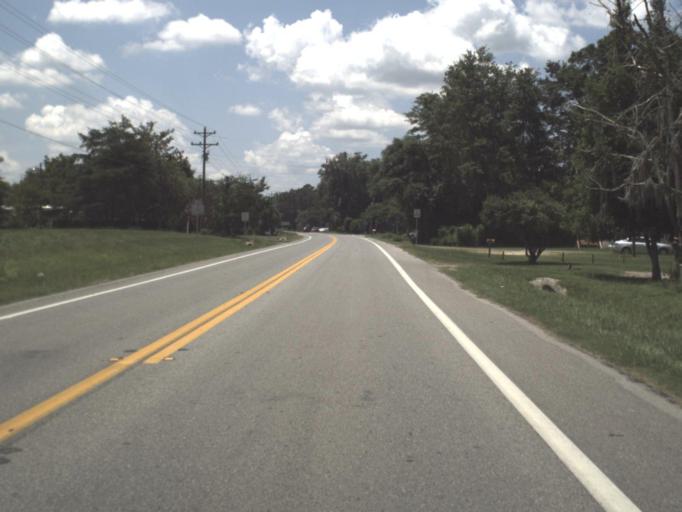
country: US
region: Florida
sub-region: Madison County
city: Madison
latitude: 30.4782
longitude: -83.6342
